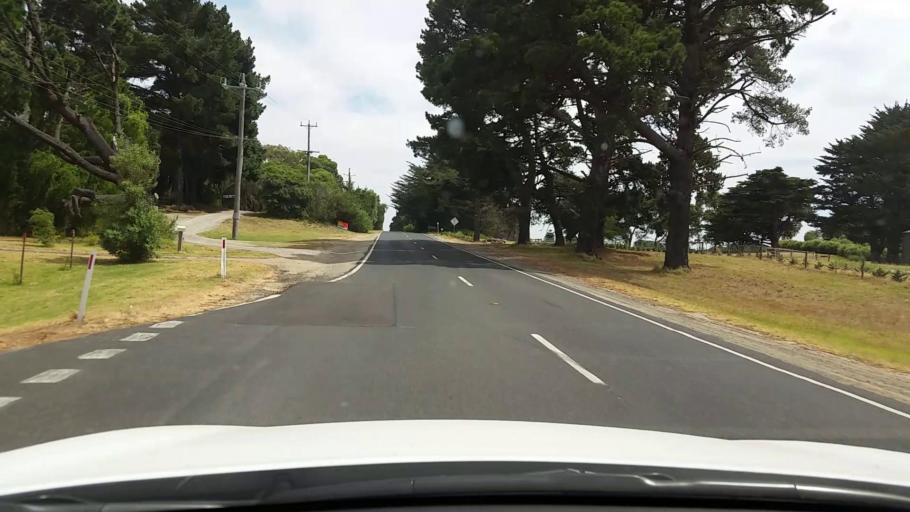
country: AU
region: Victoria
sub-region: Mornington Peninsula
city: Saint Andrews Beach
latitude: -38.4597
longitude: 144.9042
